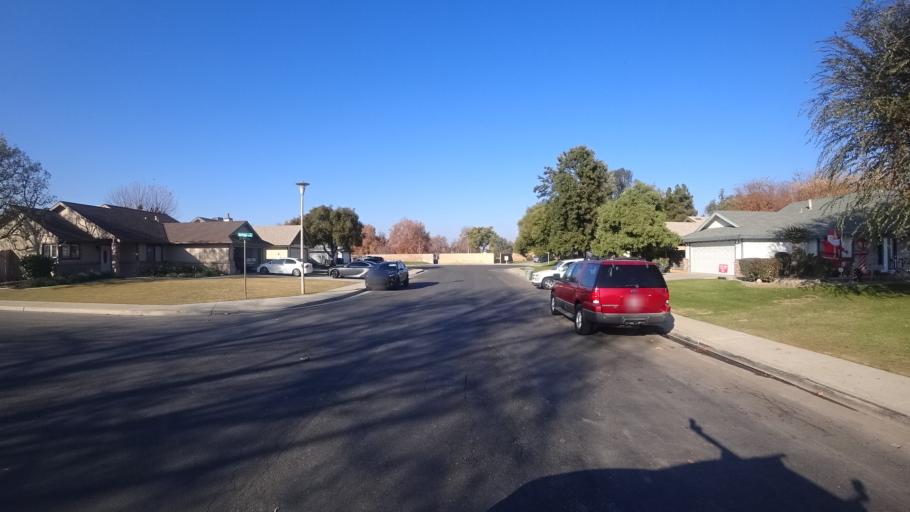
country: US
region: California
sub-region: Kern County
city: Greenacres
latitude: 35.3129
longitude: -119.0990
